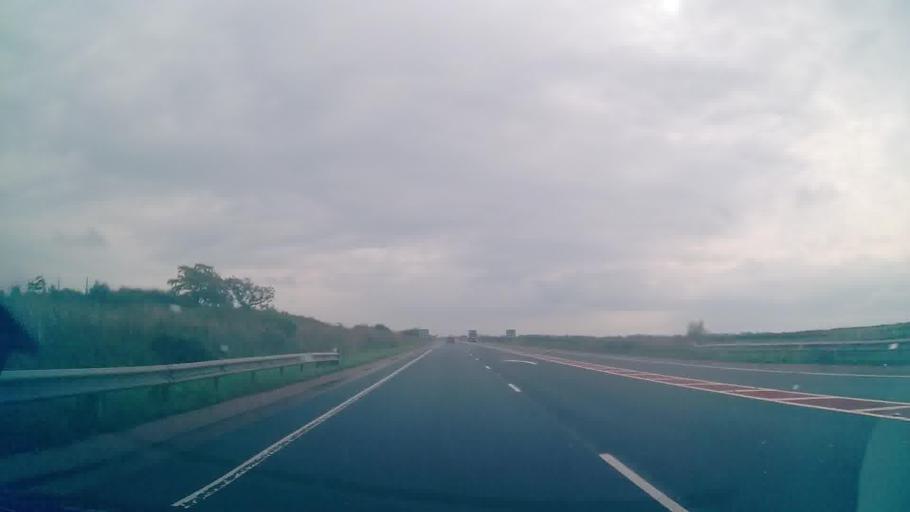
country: GB
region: Scotland
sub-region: Dumfries and Galloway
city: Lockerbie
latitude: 55.0216
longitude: -3.3720
